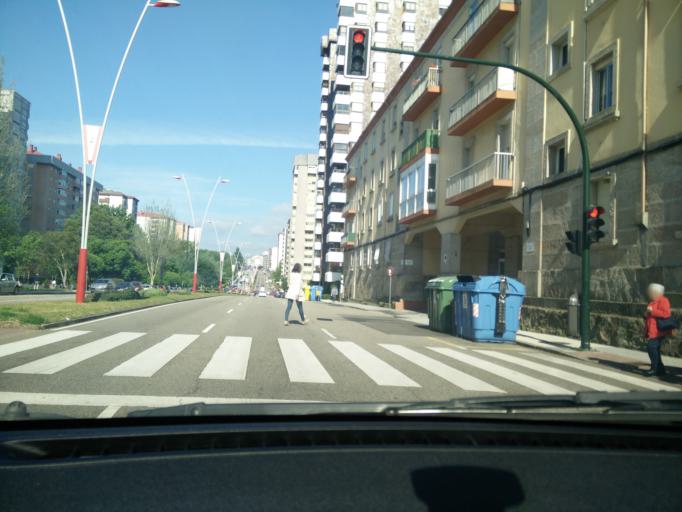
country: ES
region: Galicia
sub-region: Provincia de Pontevedra
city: Vigo
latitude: 42.2173
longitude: -8.7519
